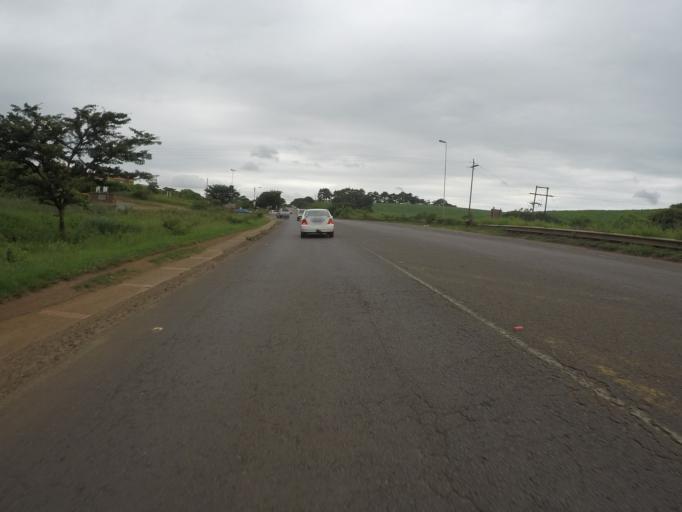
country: ZA
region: KwaZulu-Natal
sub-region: uThungulu District Municipality
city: Empangeni
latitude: -28.7781
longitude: 31.8811
